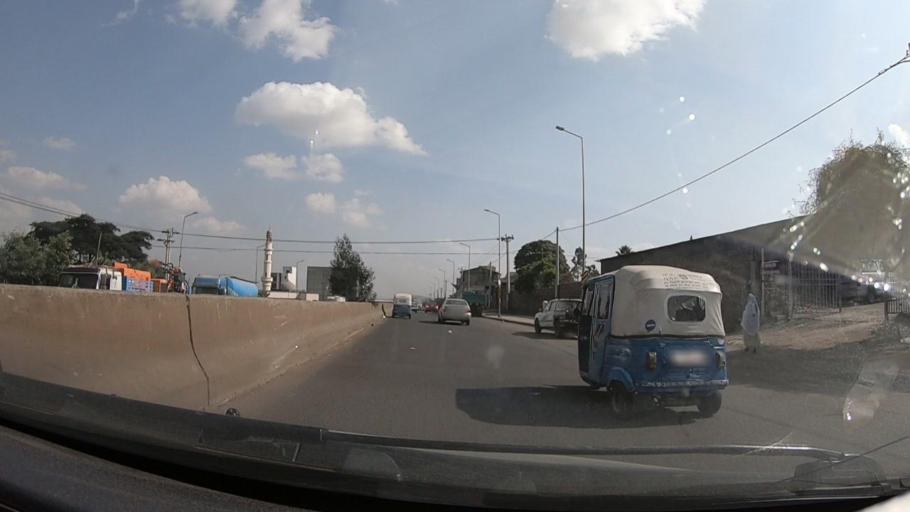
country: ET
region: Adis Abeba
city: Addis Ababa
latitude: 8.9895
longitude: 38.6913
